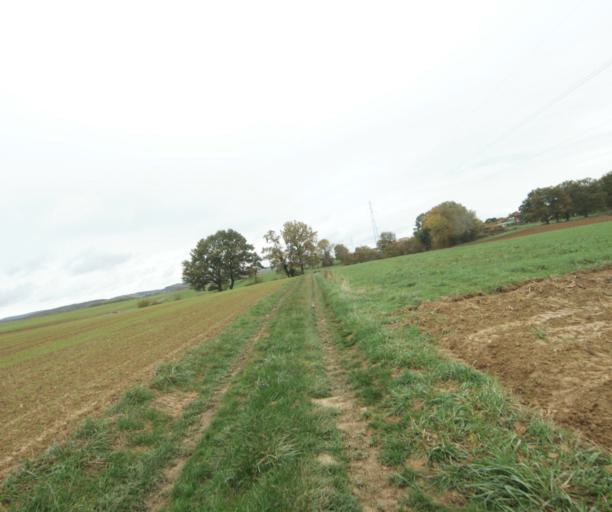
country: FR
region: Rhone-Alpes
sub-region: Departement de l'Ain
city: Pont-de-Vaux
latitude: 46.4615
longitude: 4.8672
